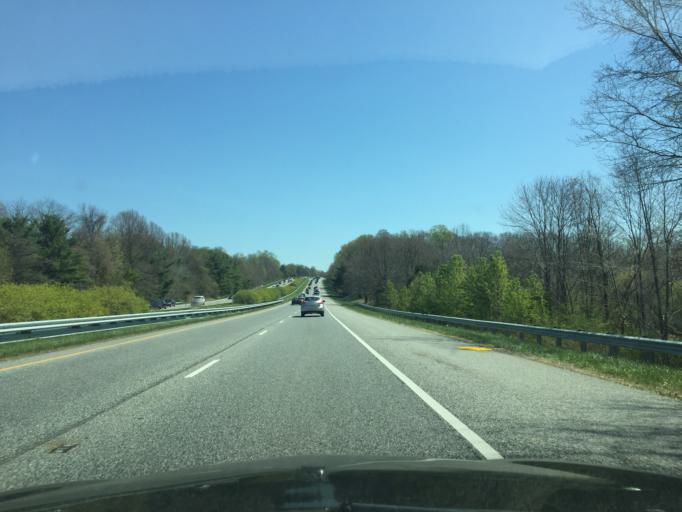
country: US
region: Maryland
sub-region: Harford County
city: Bel Air South
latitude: 39.5067
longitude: -76.3391
